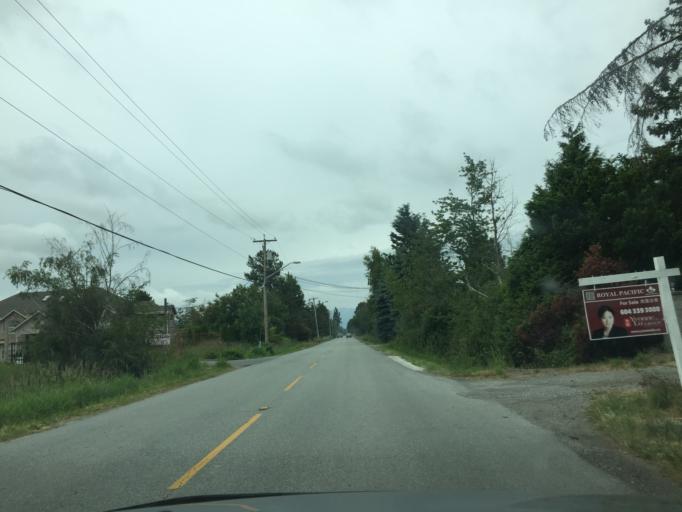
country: CA
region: British Columbia
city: Ladner
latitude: 49.1483
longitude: -123.0806
